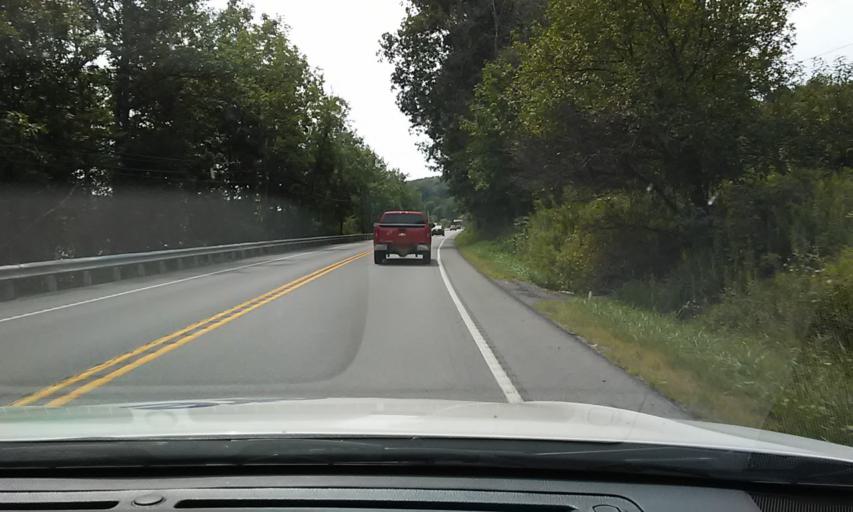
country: US
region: Pennsylvania
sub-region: Clearfield County
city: Treasure Lake
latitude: 41.1624
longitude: -78.6653
